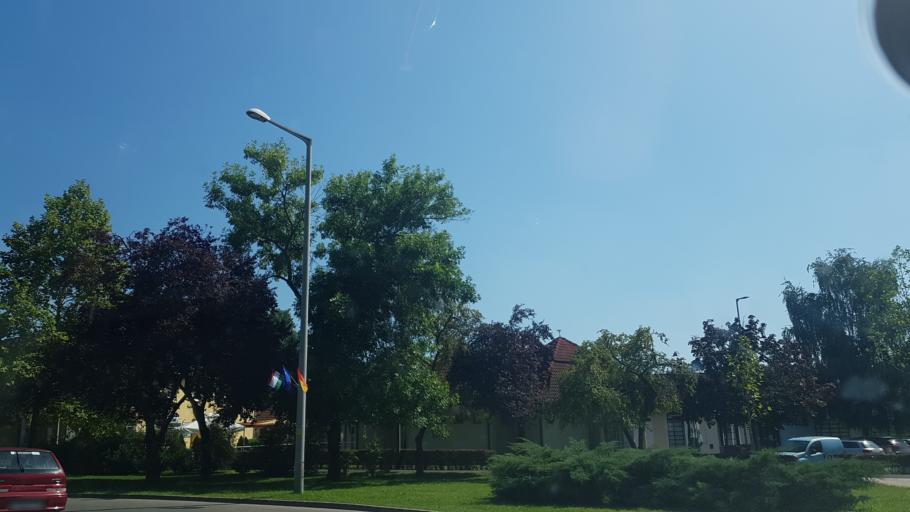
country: HU
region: Somogy
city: Nagyatad
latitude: 46.2301
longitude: 17.3568
